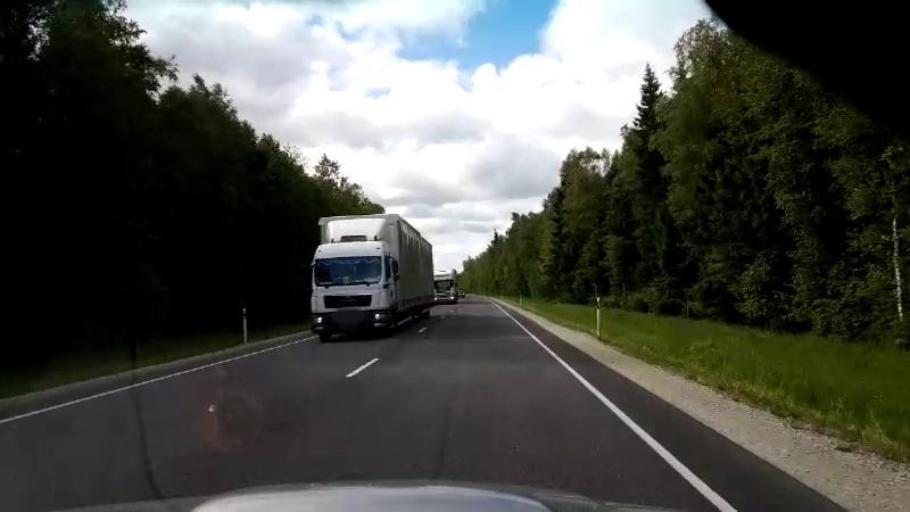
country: EE
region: Raplamaa
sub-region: Maerjamaa vald
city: Marjamaa
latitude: 58.8242
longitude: 24.4143
